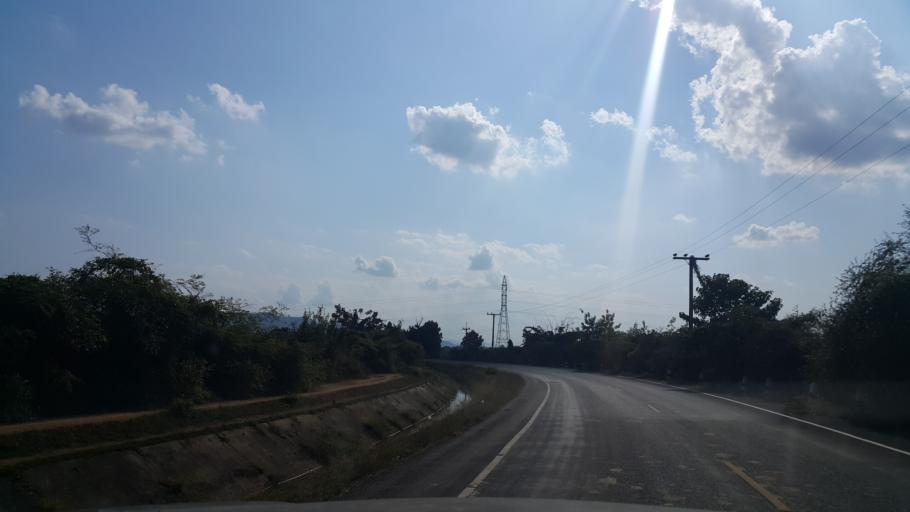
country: TH
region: Lamphun
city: Mae Tha
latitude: 18.5385
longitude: 99.0959
